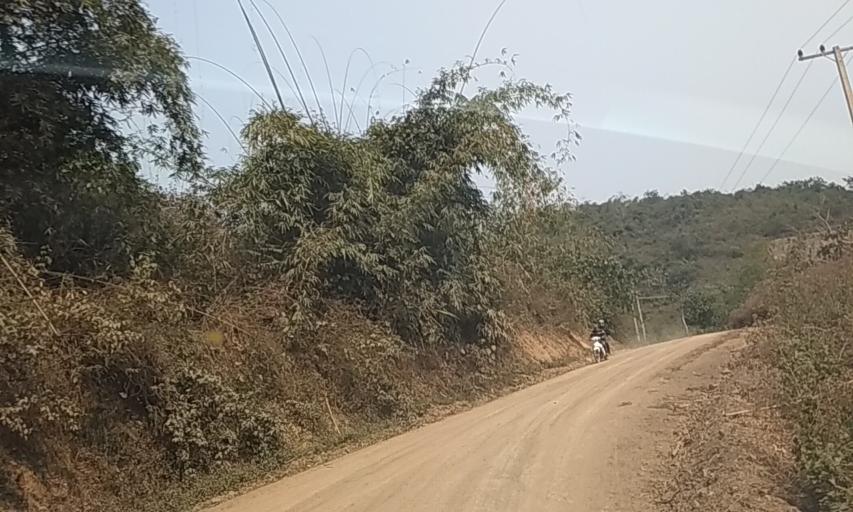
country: VN
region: Huyen Dien Bien
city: Dien Bien Phu
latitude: 21.4204
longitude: 102.7586
